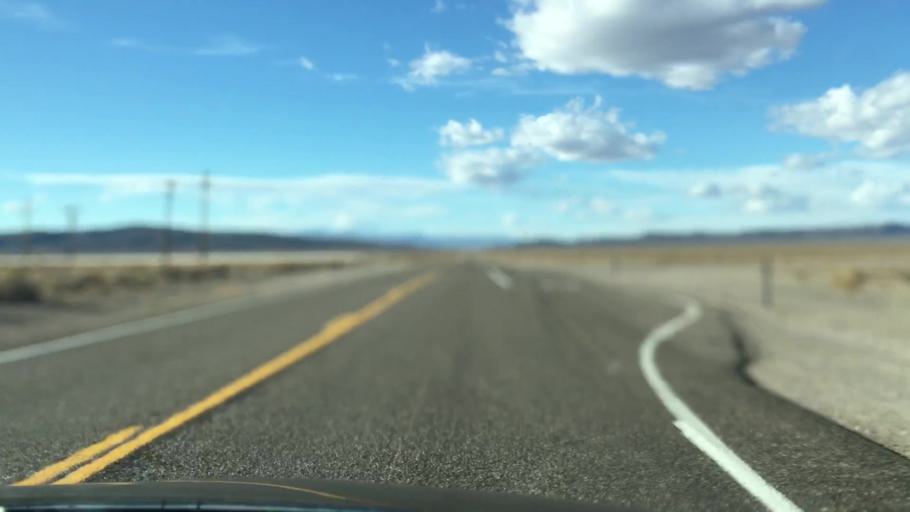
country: US
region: Nevada
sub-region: Nye County
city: Beatty
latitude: 37.1380
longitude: -116.8546
